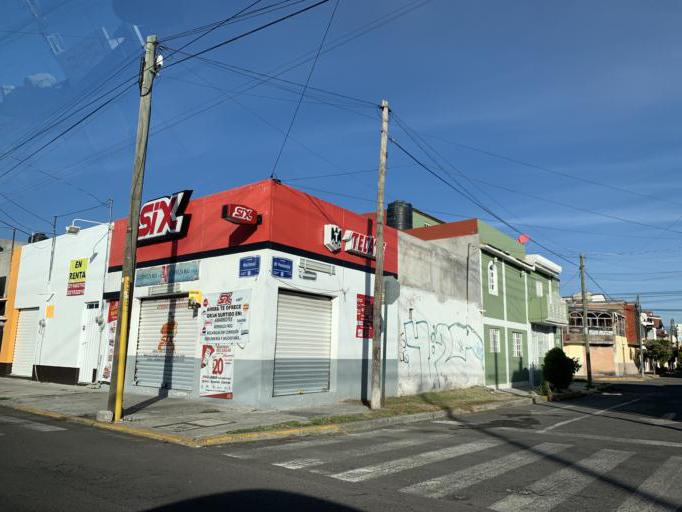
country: MX
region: Puebla
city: Puebla
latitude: 19.0064
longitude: -98.2328
